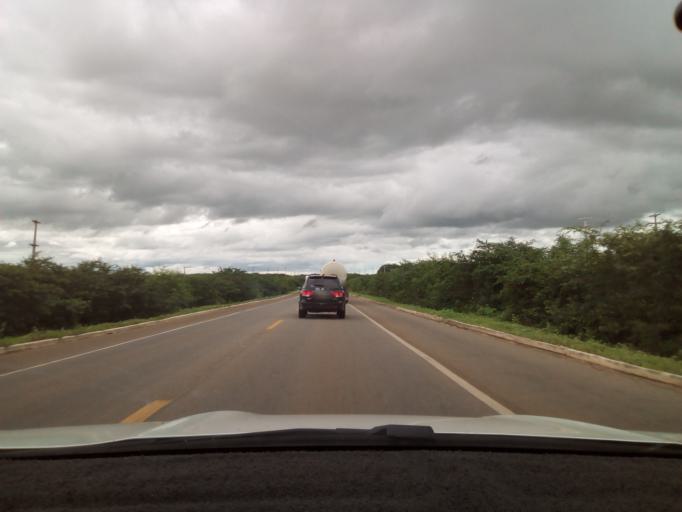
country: BR
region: Rio Grande do Norte
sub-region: Barauna
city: Barauna
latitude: -4.9325
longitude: -37.4138
